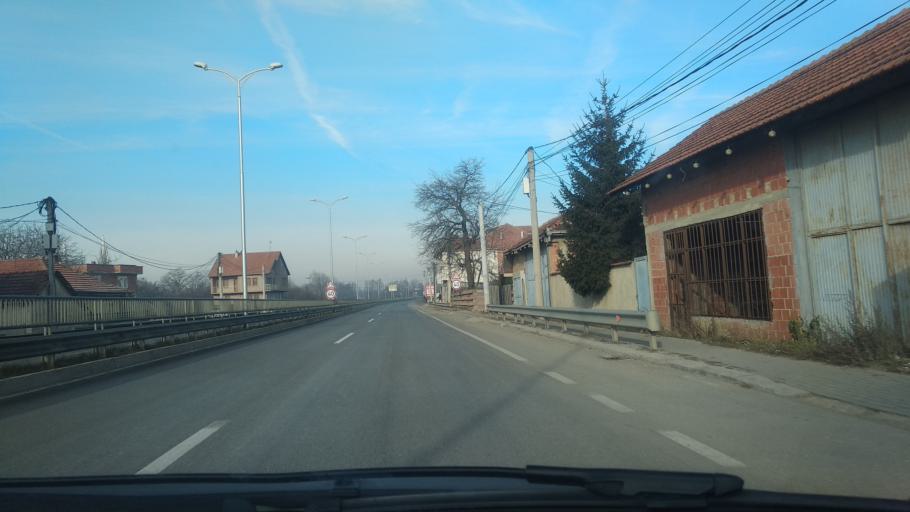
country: XK
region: Pristina
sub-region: Komuna e Obiliqit
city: Obiliq
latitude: 42.7241
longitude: 21.0822
